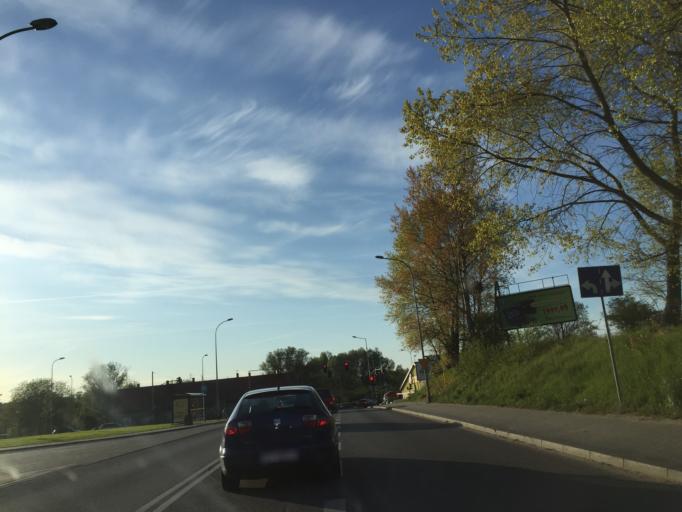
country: PL
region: Pomeranian Voivodeship
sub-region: Powiat gdanski
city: Kowale
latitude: 54.3243
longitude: 18.5497
